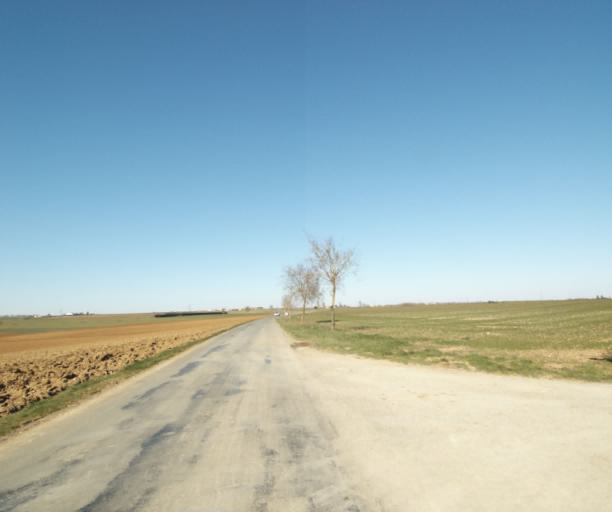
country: FR
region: Poitou-Charentes
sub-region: Departement des Deux-Sevres
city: Bessines
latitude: 46.3375
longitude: -0.5141
